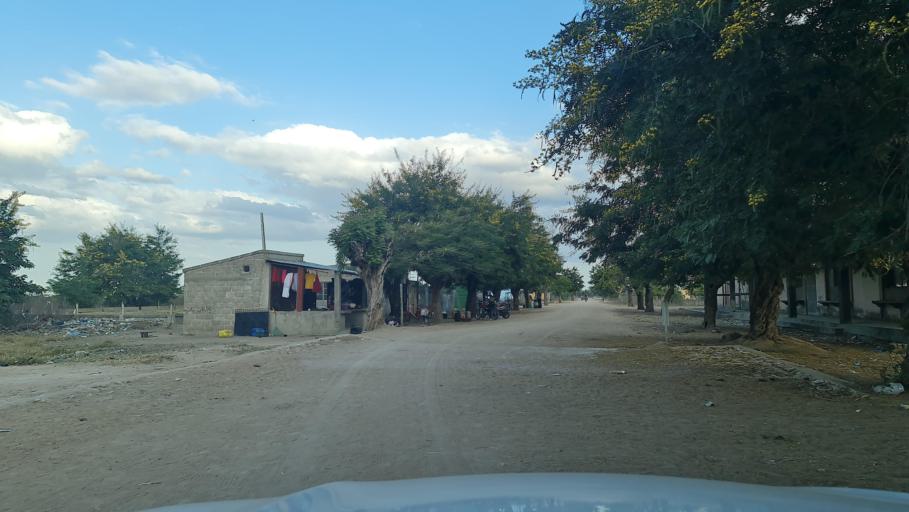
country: EG
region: Aswan
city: Kawm Umbu
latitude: 24.2796
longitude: 33.5664
